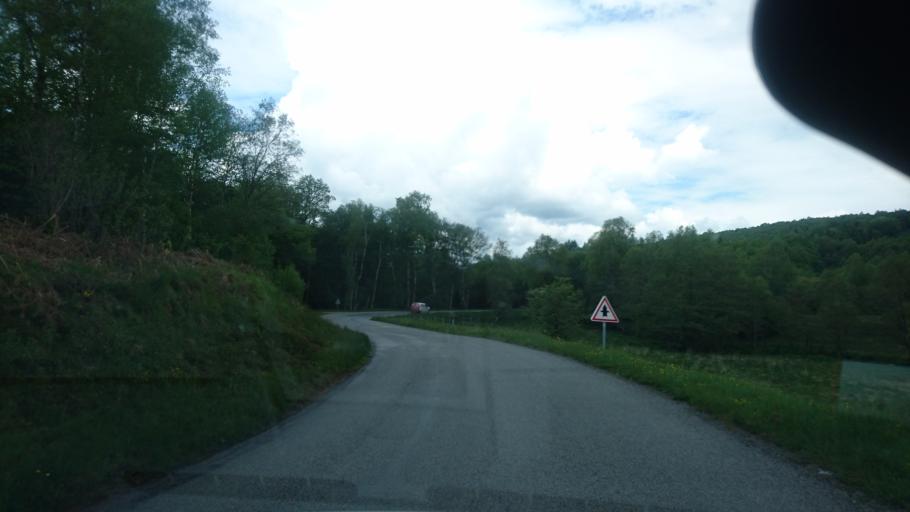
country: FR
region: Limousin
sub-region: Departement de la Haute-Vienne
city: Peyrat-le-Chateau
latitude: 45.7904
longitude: 1.9223
